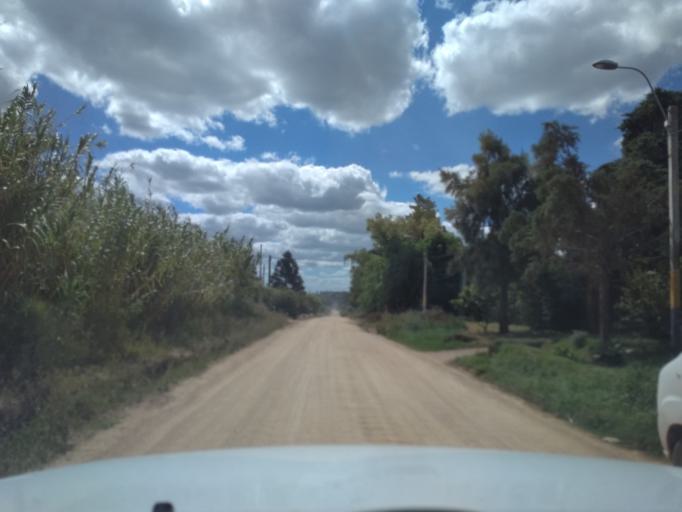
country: UY
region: Canelones
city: Colonia Nicolich
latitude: -34.8298
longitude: -55.9915
